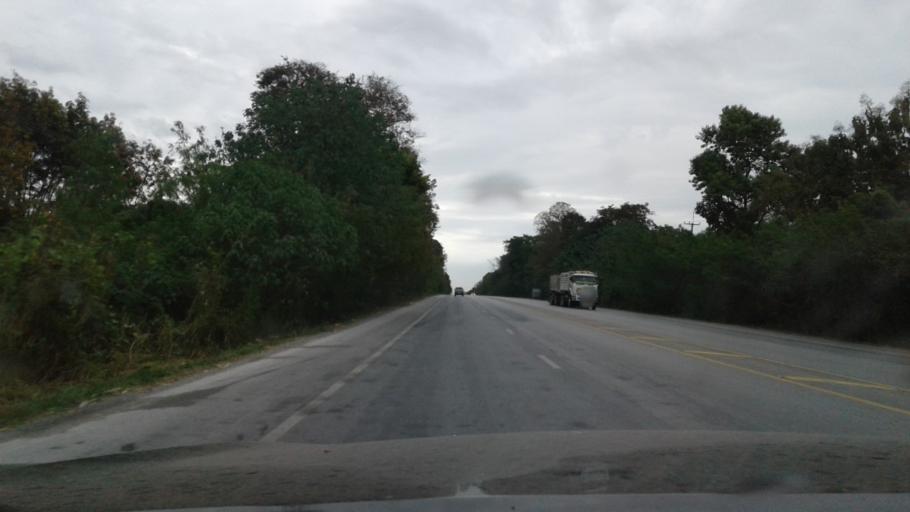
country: TH
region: Changwat Udon Thani
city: Nong Wua So
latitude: 17.2501
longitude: 102.5671
